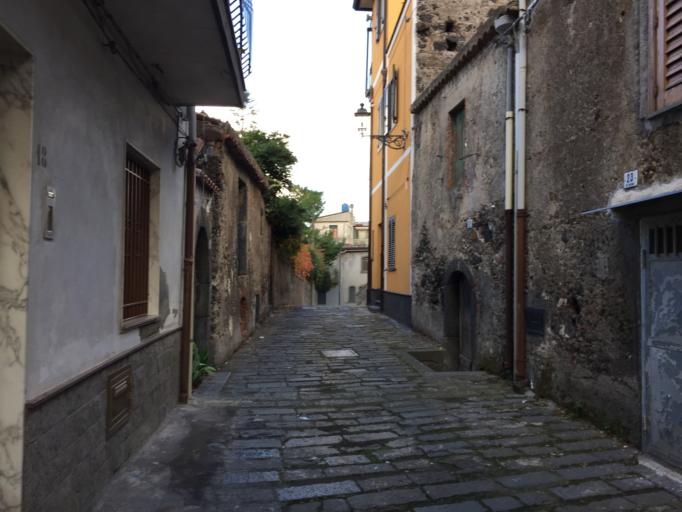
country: IT
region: Sicily
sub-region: Catania
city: Randazzo
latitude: 37.8767
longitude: 14.9448
